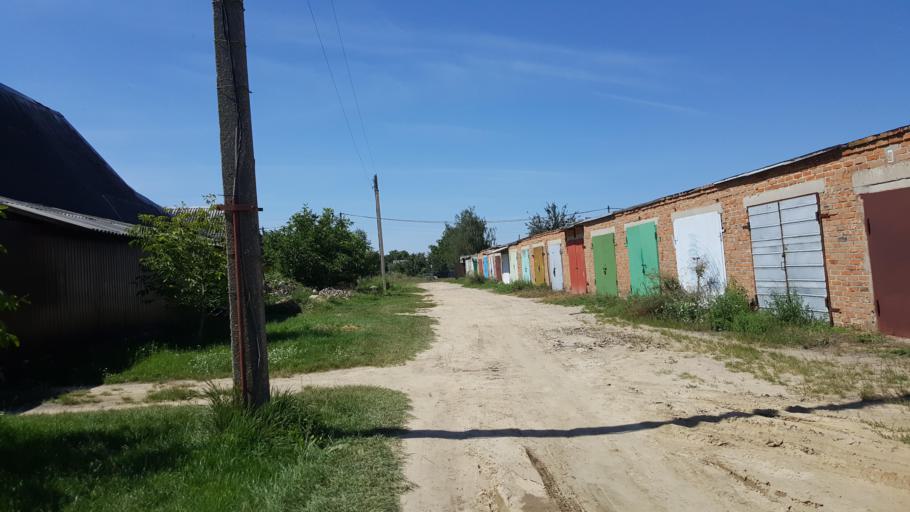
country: BY
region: Brest
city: Charnawchytsy
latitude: 52.2650
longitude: 23.5856
